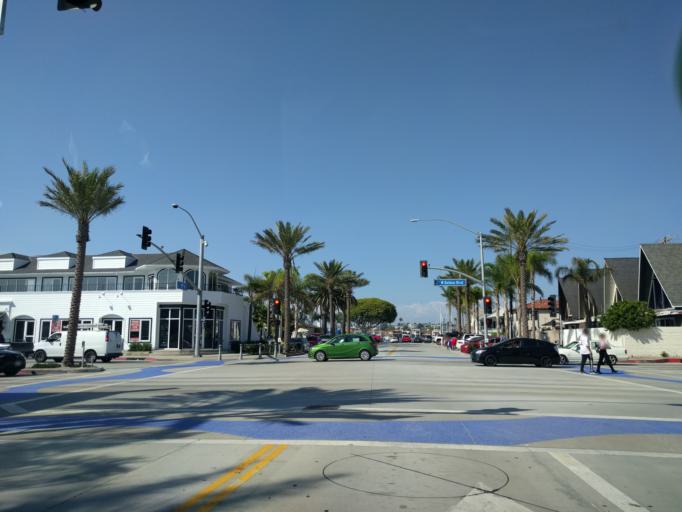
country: US
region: California
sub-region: Orange County
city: Newport Beach
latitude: 33.6068
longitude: -117.9207
